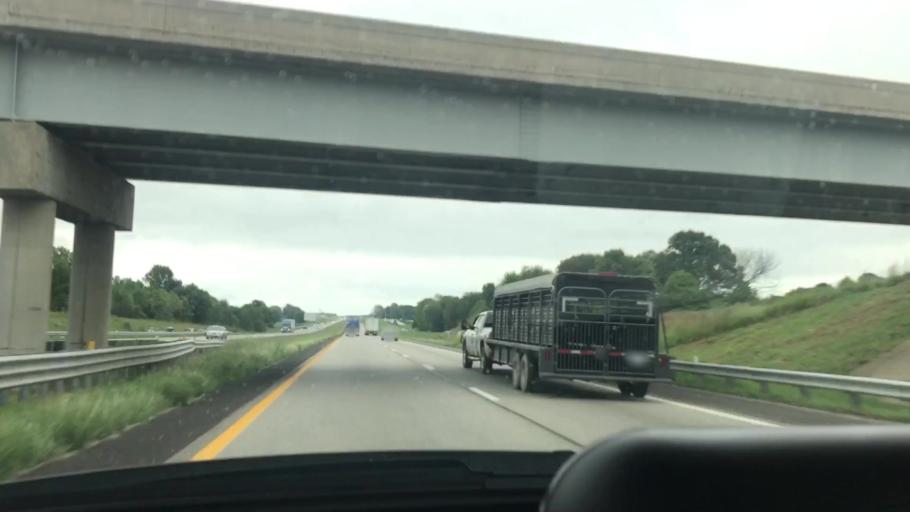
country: US
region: Missouri
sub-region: Greene County
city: Republic
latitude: 37.1960
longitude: -93.4444
